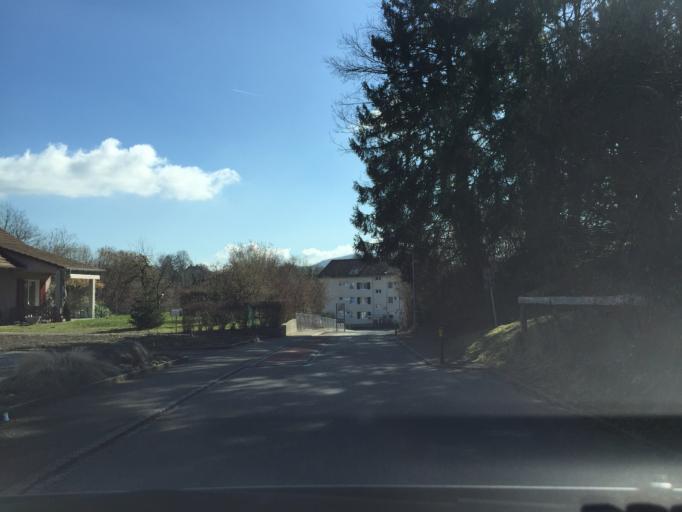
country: CH
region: Thurgau
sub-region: Frauenfeld District
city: Diessenhofen
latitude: 47.6888
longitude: 8.7458
